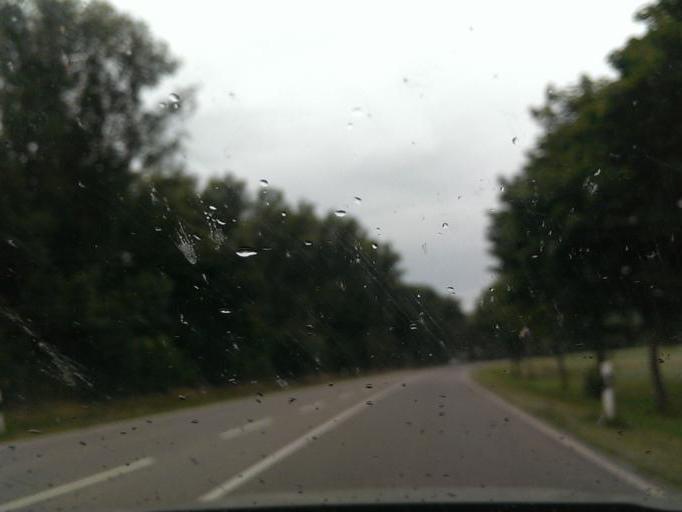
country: DE
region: Bavaria
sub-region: Upper Bavaria
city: Denkendorf
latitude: 49.0044
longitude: 11.4466
